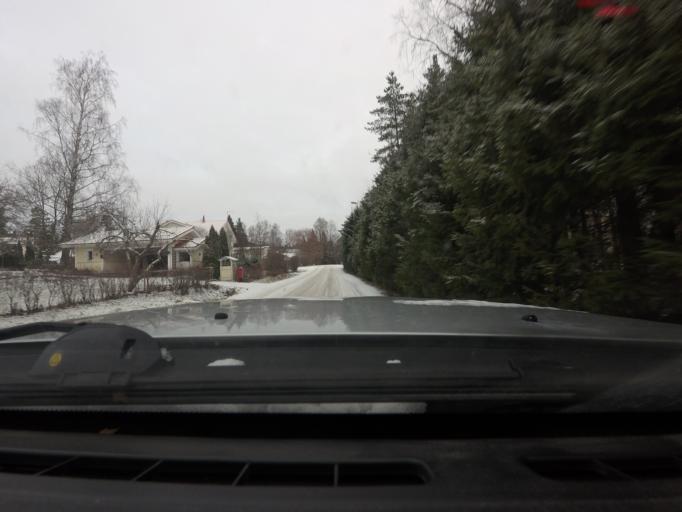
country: FI
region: Uusimaa
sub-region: Helsinki
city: Kilo
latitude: 60.2241
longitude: 24.7759
